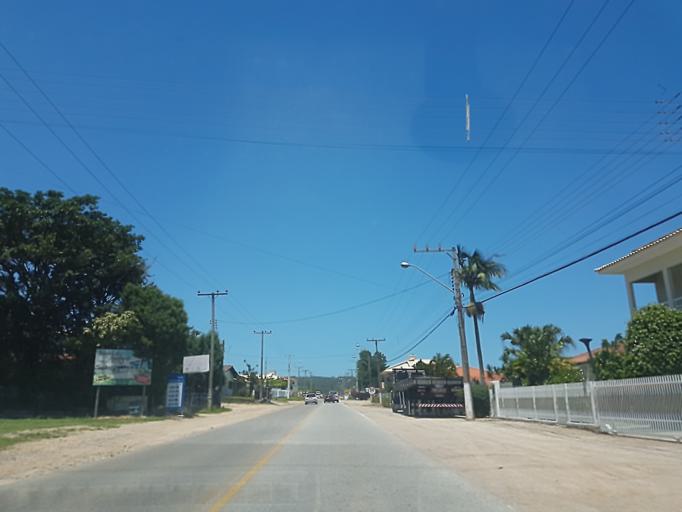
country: BR
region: Santa Catarina
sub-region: Jaguaruna
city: Jaguaruna
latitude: -28.6008
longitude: -49.0499
